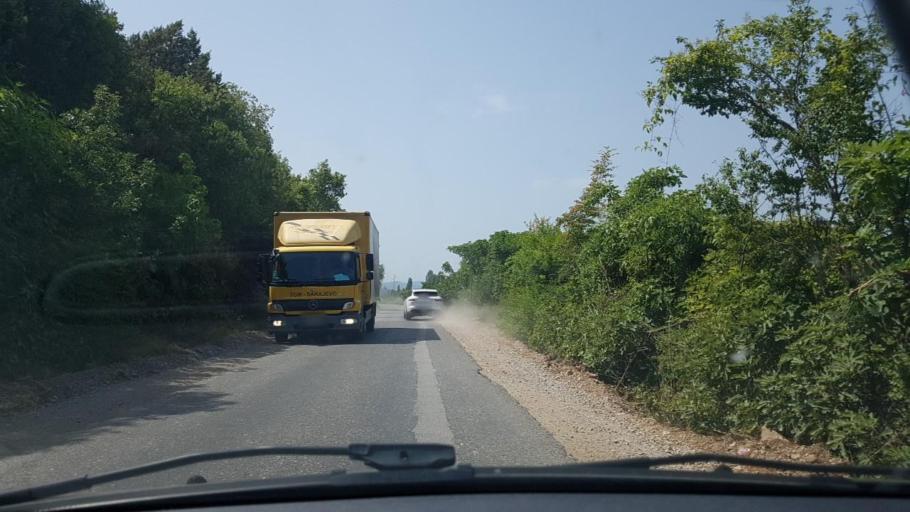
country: BA
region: Federation of Bosnia and Herzegovina
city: Tasovcici
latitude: 43.0325
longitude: 17.7383
